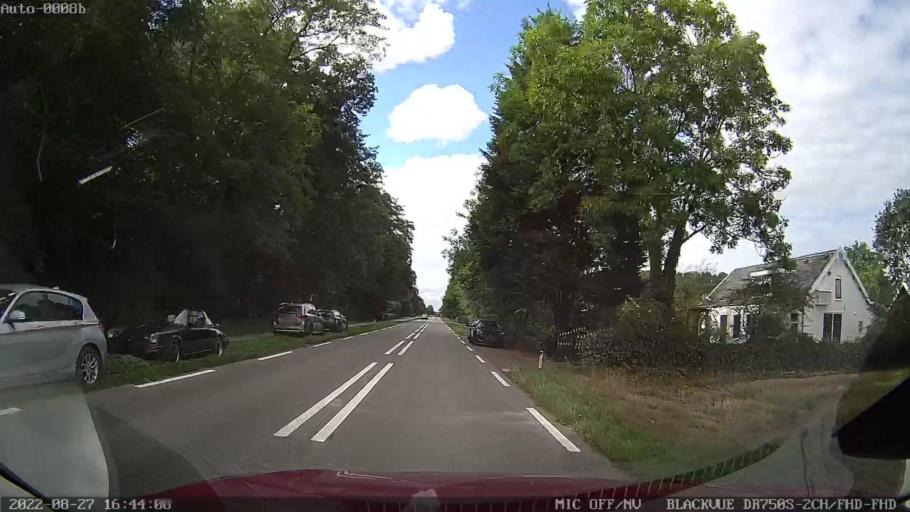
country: NL
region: Zeeland
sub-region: Schouwen-Duiveland
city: Scharendijke
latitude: 51.6798
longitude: 3.9473
